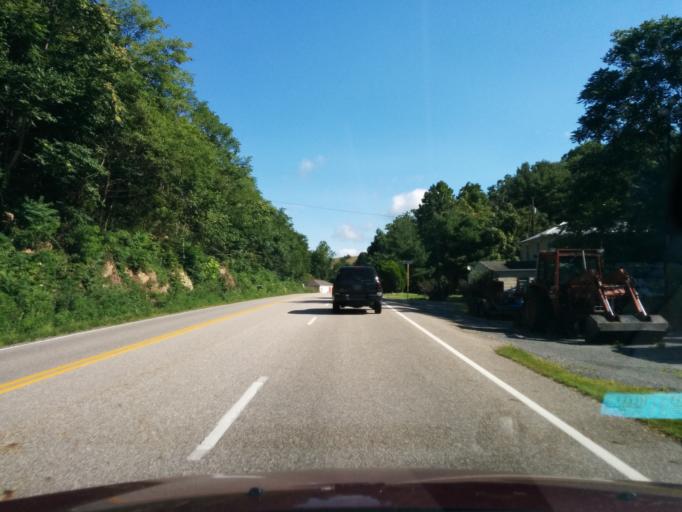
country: US
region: Virginia
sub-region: City of Lexington
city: Lexington
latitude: 37.7442
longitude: -79.4587
